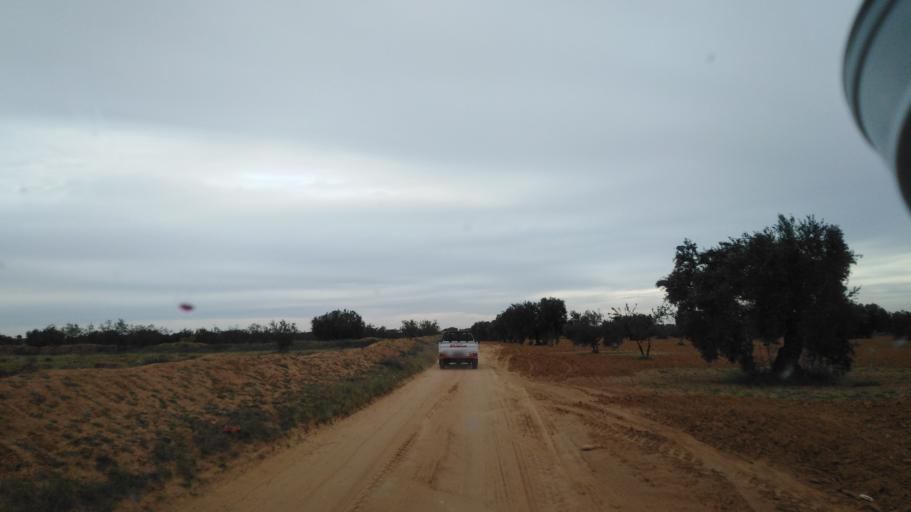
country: TN
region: Safaqis
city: Bi'r `Ali Bin Khalifah
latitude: 34.7769
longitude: 10.3679
